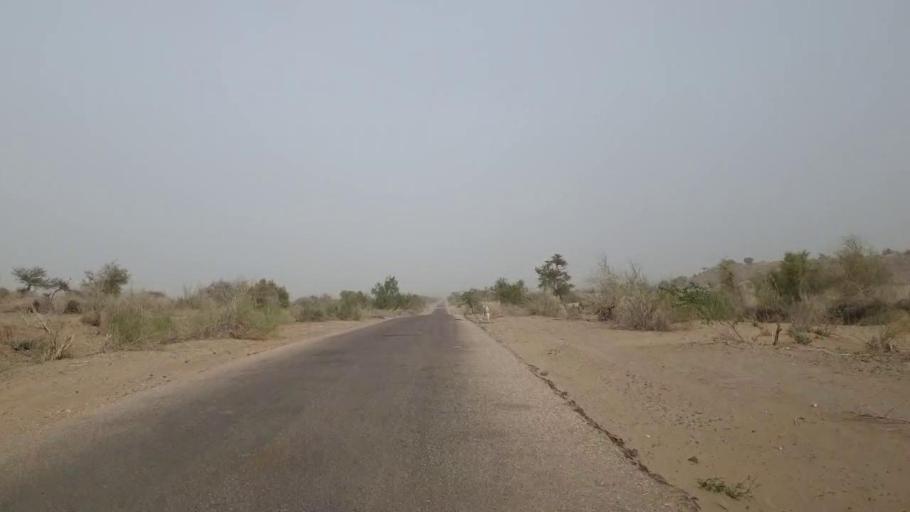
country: PK
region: Sindh
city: Islamkot
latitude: 24.5794
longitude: 70.3056
